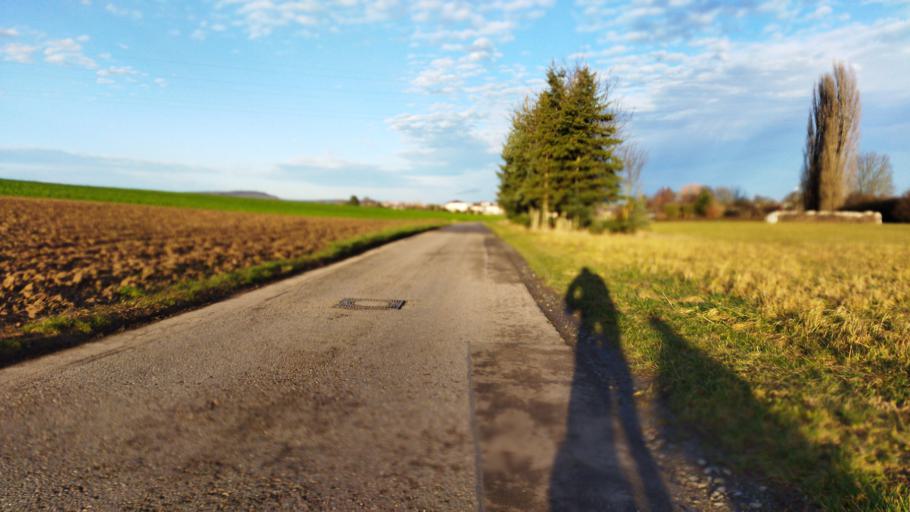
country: DE
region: Baden-Wuerttemberg
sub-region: Regierungsbezirk Stuttgart
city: Brackenheim
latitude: 49.0592
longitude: 9.0590
